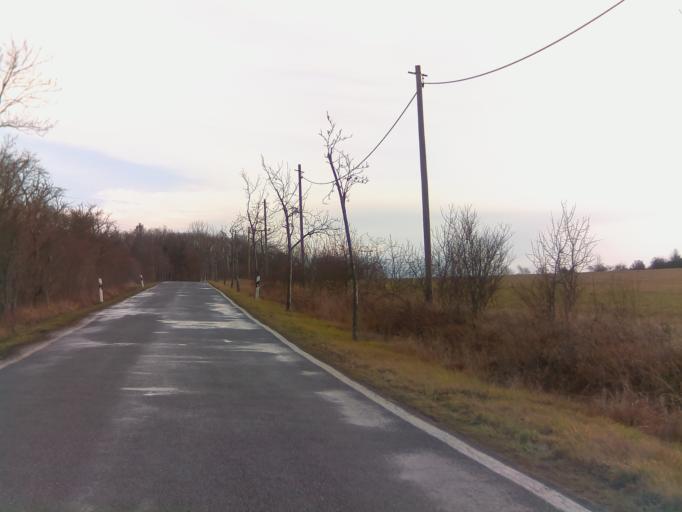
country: DE
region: Thuringia
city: Bad Berka
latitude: 50.9229
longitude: 11.2754
